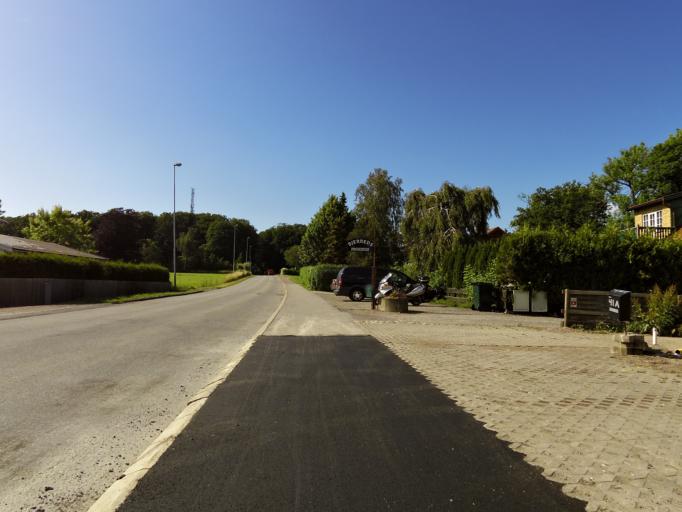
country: SE
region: Skane
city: Bjarred
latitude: 55.7091
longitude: 13.0349
